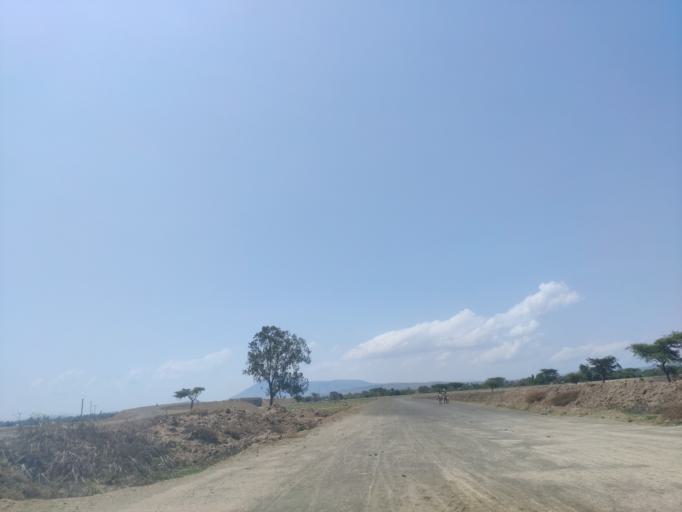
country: ET
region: Oromiya
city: Mojo
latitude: 8.3029
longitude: 38.9319
